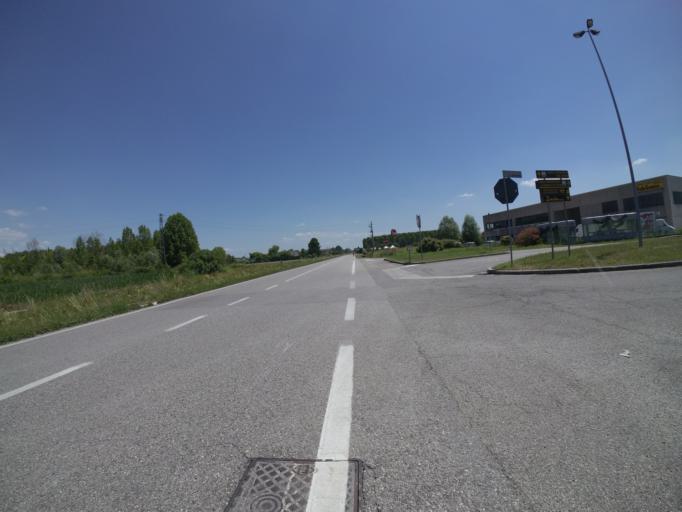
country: IT
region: Friuli Venezia Giulia
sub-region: Provincia di Udine
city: Rivignano
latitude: 45.8801
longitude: 13.0269
